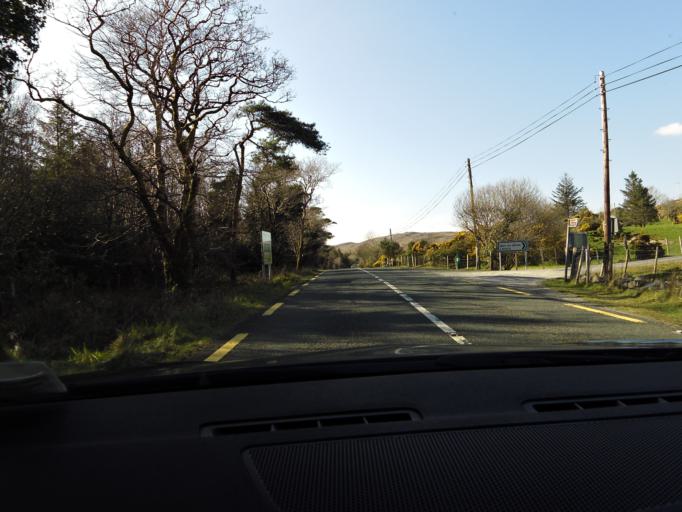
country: IE
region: Connaught
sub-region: County Galway
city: Clifden
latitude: 53.4736
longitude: -9.8812
